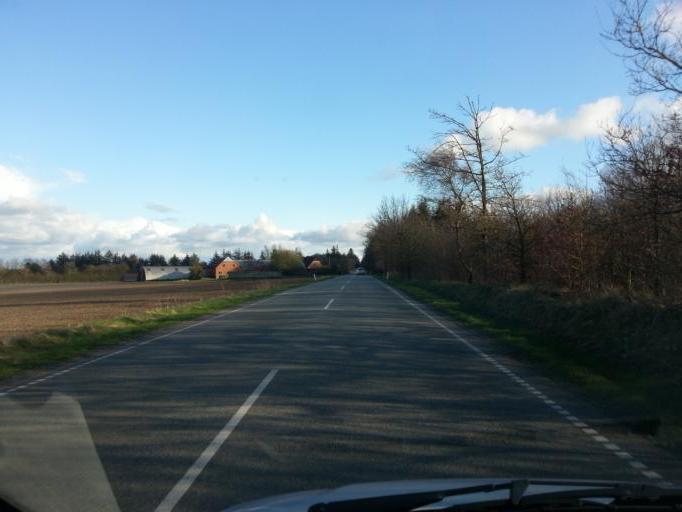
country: DK
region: Central Jutland
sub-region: Ringkobing-Skjern Kommune
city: Tarm
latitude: 55.8435
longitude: 8.5588
